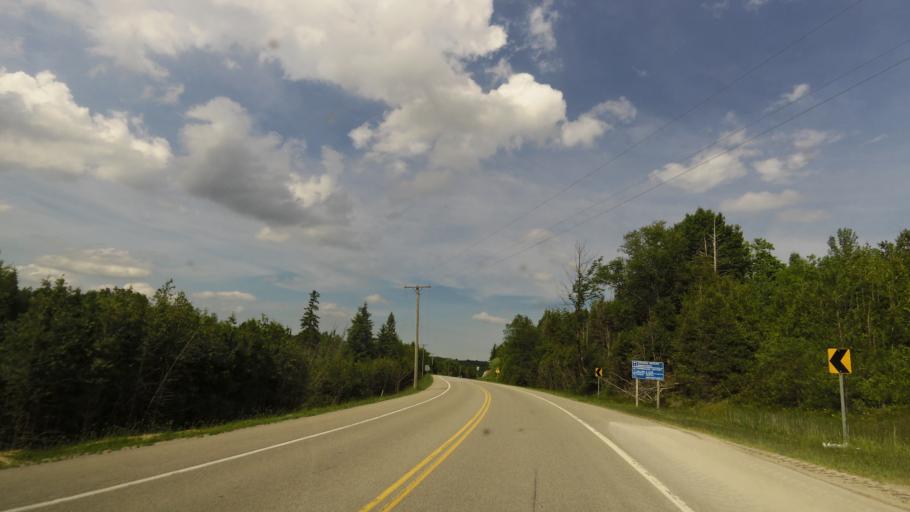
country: CA
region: Ontario
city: Orangeville
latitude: 43.9495
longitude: -80.0896
